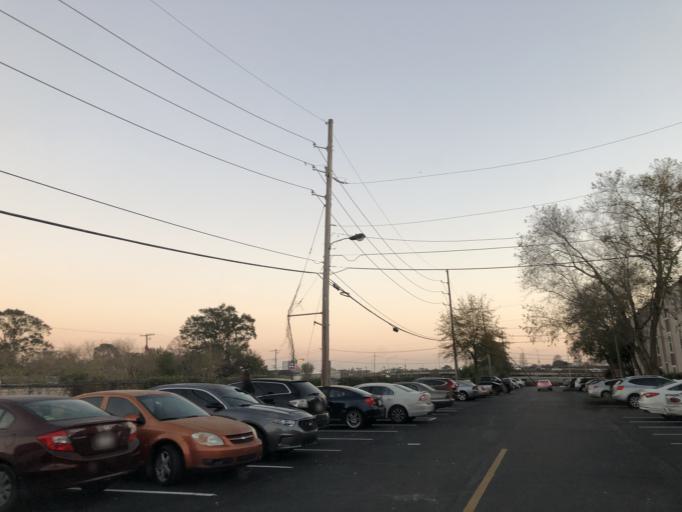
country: US
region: Louisiana
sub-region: Jefferson Parish
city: Kenner
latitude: 30.0083
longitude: -90.2104
